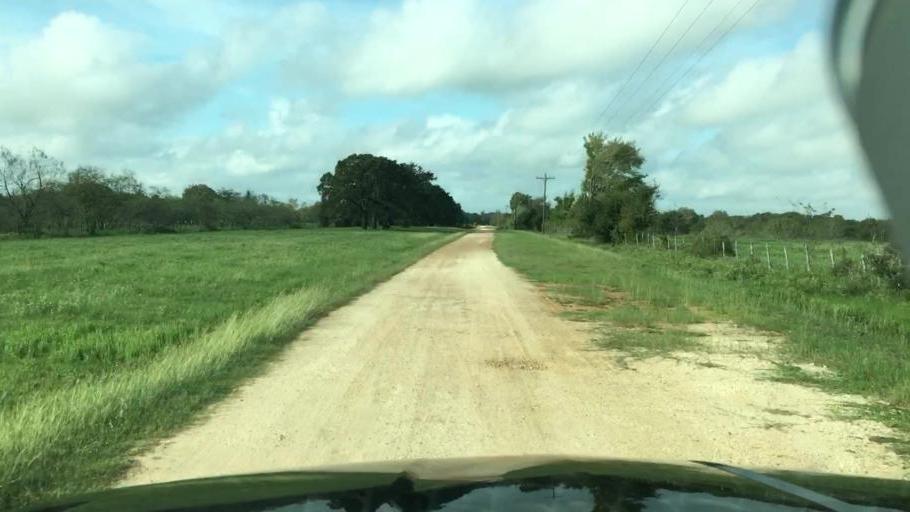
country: US
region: Texas
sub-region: Burleson County
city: Somerville
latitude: 30.3006
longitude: -96.7333
